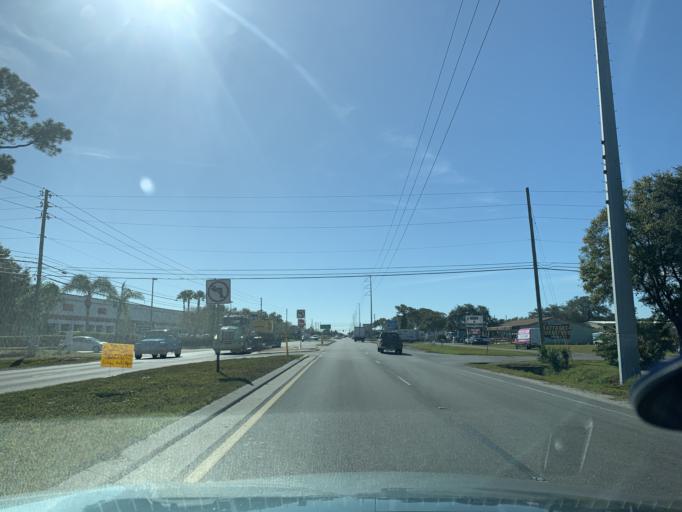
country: US
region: Florida
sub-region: Pinellas County
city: Largo
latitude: 27.8913
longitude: -82.7625
